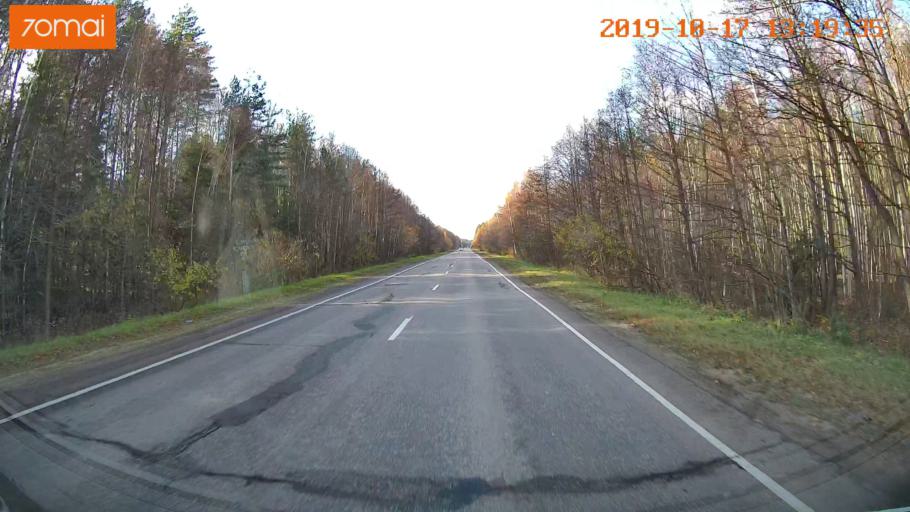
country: RU
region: Rjazan
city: Gus'-Zheleznyy
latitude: 55.0704
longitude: 41.0705
